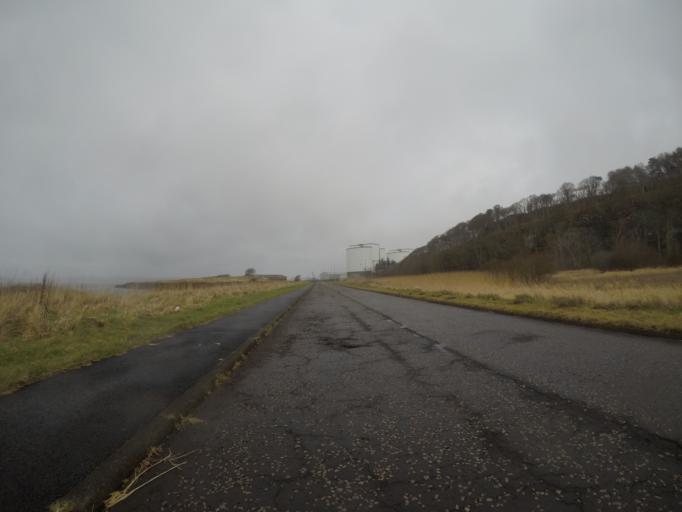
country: GB
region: Scotland
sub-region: North Ayrshire
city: Millport
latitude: 55.7163
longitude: -4.9019
